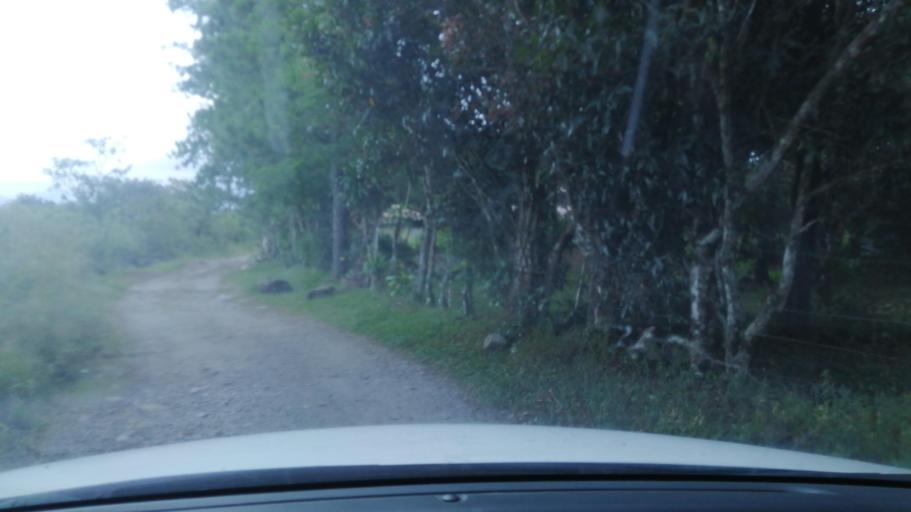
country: PA
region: Chiriqui
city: Potrerillos Arriba
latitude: 8.6857
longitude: -82.4542
